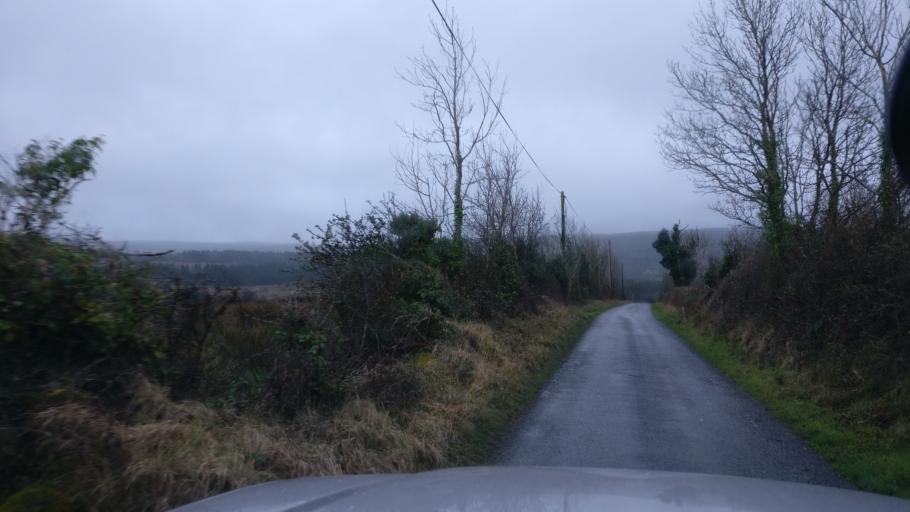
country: IE
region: Connaught
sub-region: County Galway
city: Loughrea
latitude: 53.1557
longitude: -8.6373
